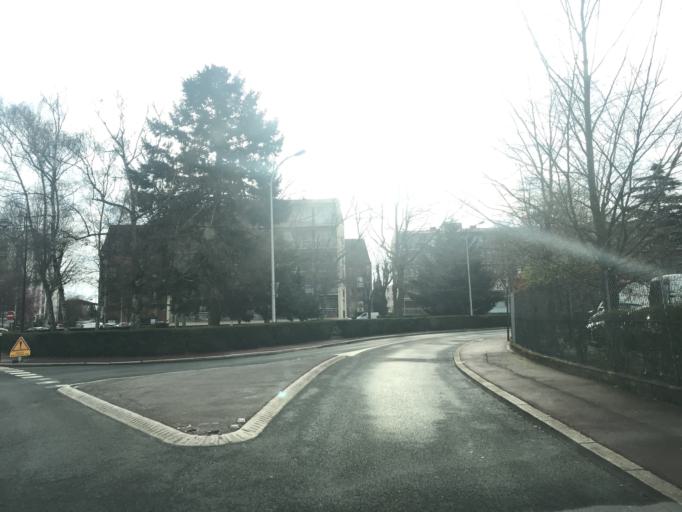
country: FR
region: Ile-de-France
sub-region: Departement des Yvelines
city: Velizy-Villacoublay
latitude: 48.7827
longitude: 2.1865
